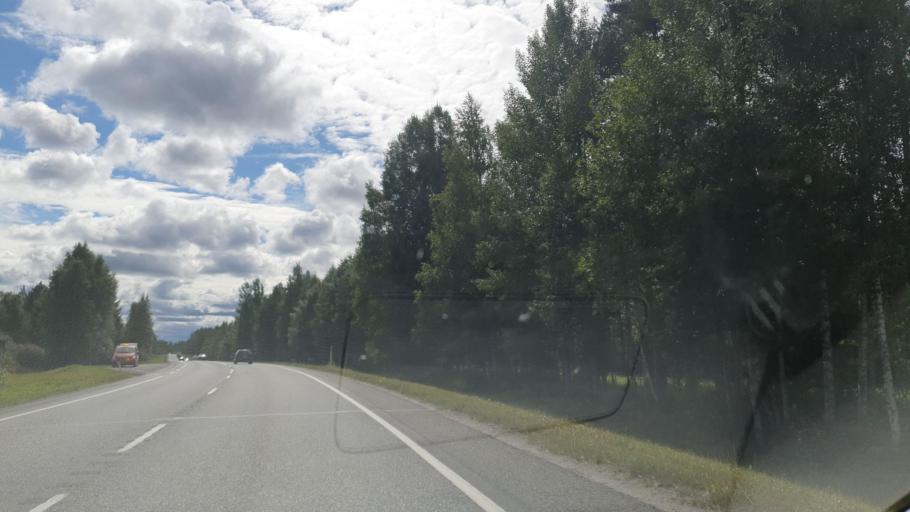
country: FI
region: Kainuu
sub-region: Kajaani
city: Kajaani
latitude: 64.1463
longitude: 27.5030
